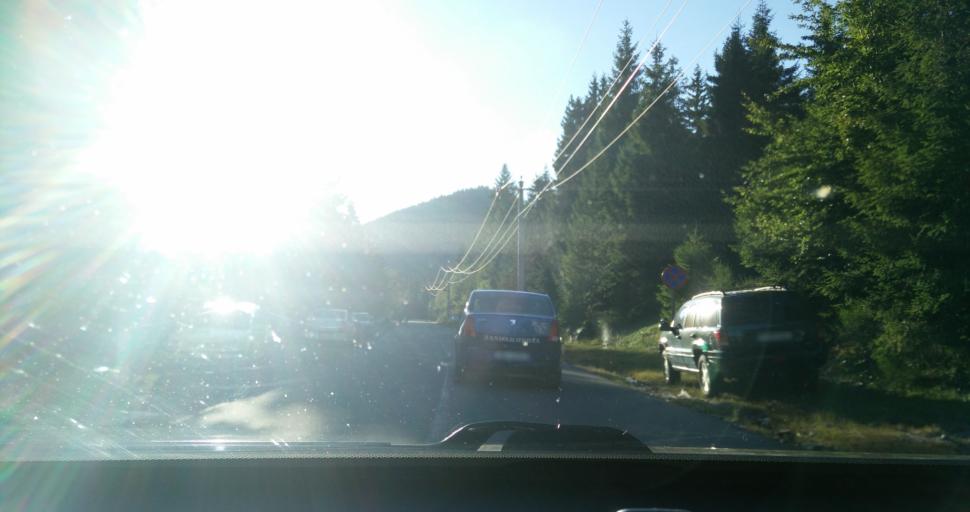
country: RO
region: Bihor
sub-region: Oras Nucet
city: Nucet
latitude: 46.5161
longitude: 22.6670
